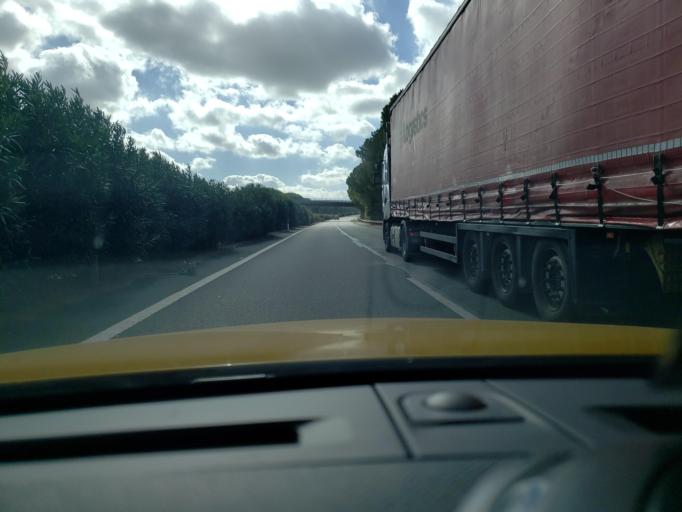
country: ES
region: Andalusia
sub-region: Provincia de Sevilla
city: Lebrija
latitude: 36.8654
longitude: -5.9942
